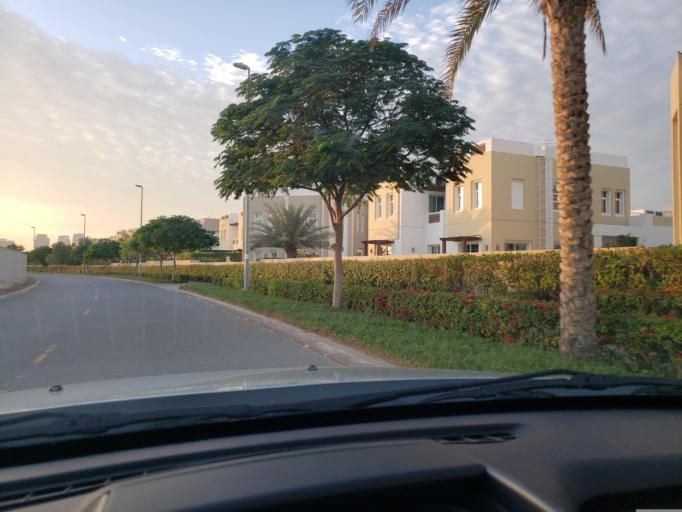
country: AE
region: Dubai
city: Dubai
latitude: 25.0222
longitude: 55.2685
